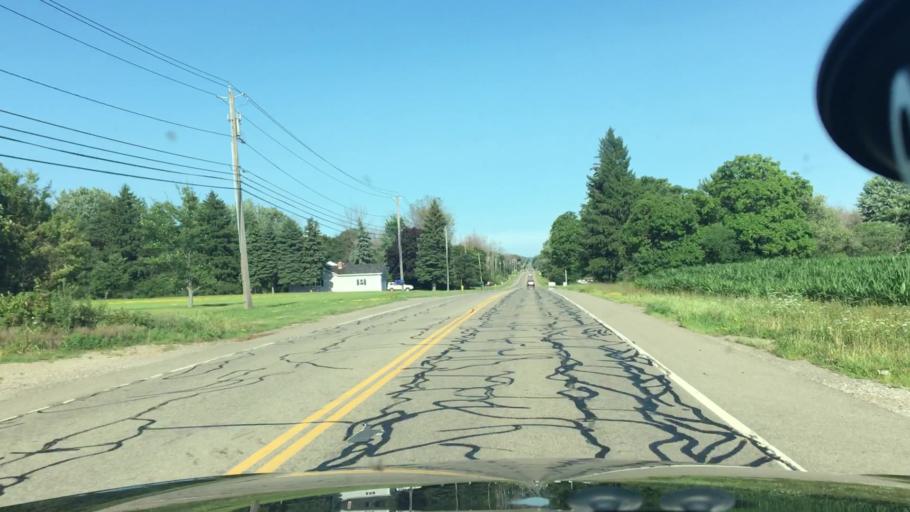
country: US
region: New York
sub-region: Erie County
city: Angola
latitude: 42.6525
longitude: -78.9996
